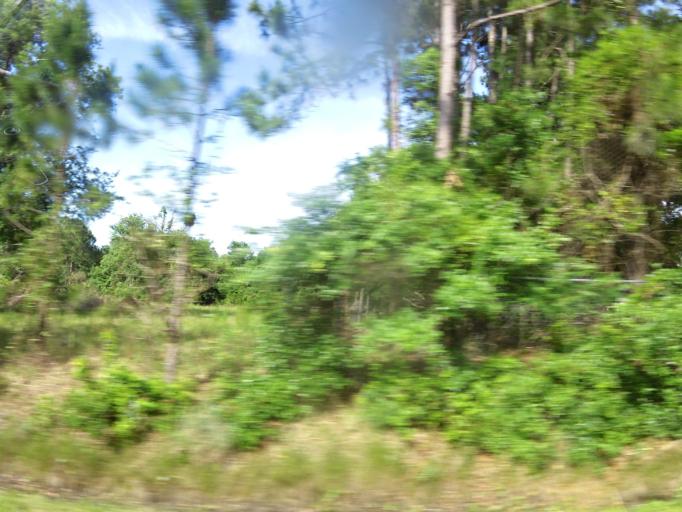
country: US
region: Florida
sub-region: Nassau County
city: Fernandina Beach
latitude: 30.5124
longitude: -81.4769
